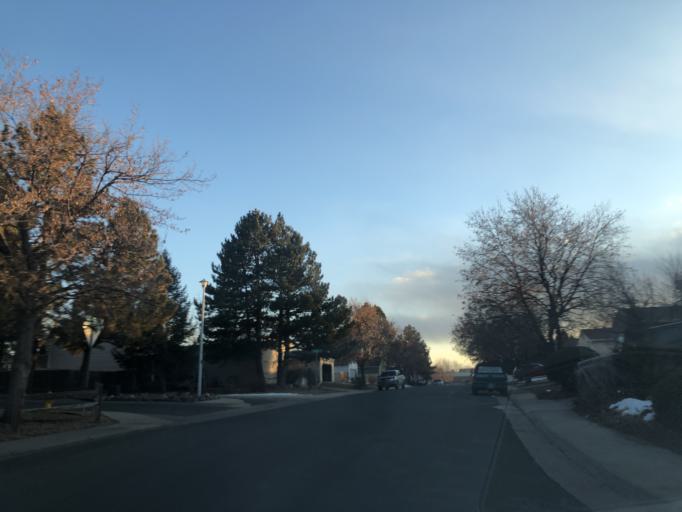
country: US
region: Colorado
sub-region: Adams County
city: Aurora
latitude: 39.7055
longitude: -104.8022
